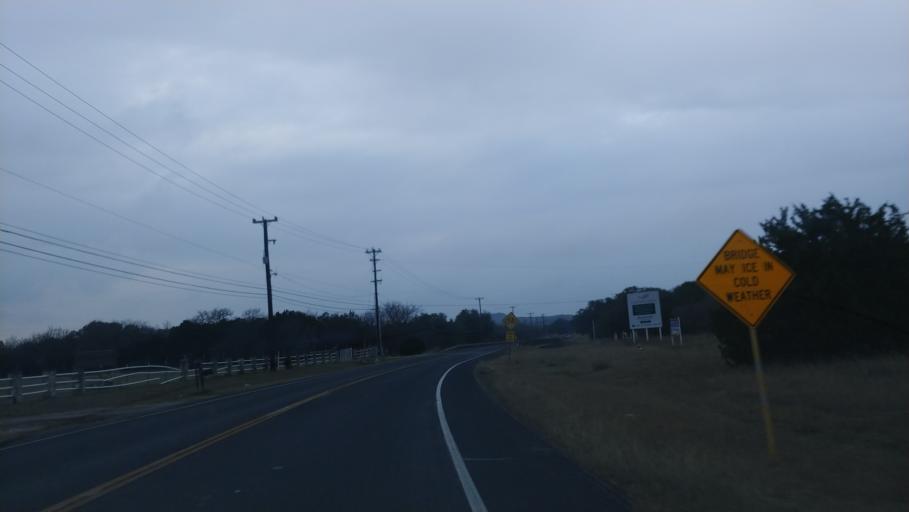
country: US
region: Texas
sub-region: Bexar County
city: Cross Mountain
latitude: 29.6778
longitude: -98.6660
